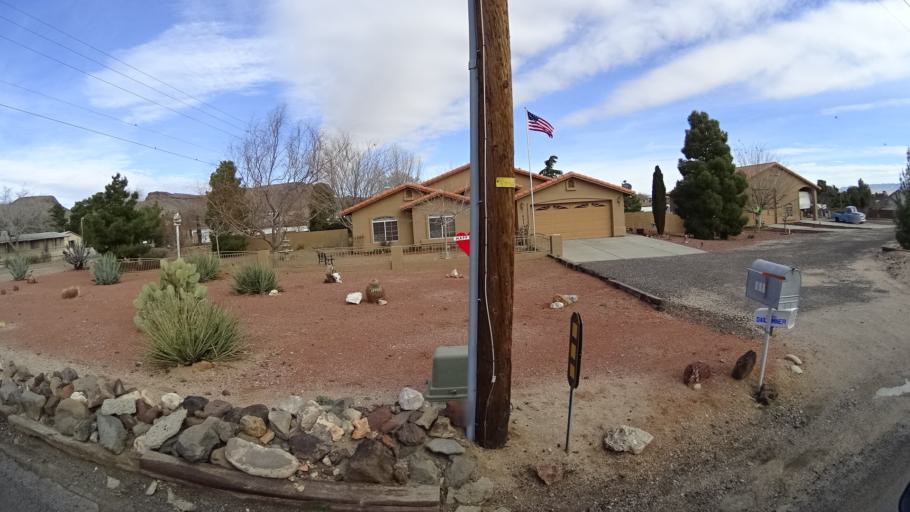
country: US
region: Arizona
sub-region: Mohave County
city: New Kingman-Butler
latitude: 35.2293
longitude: -114.0489
